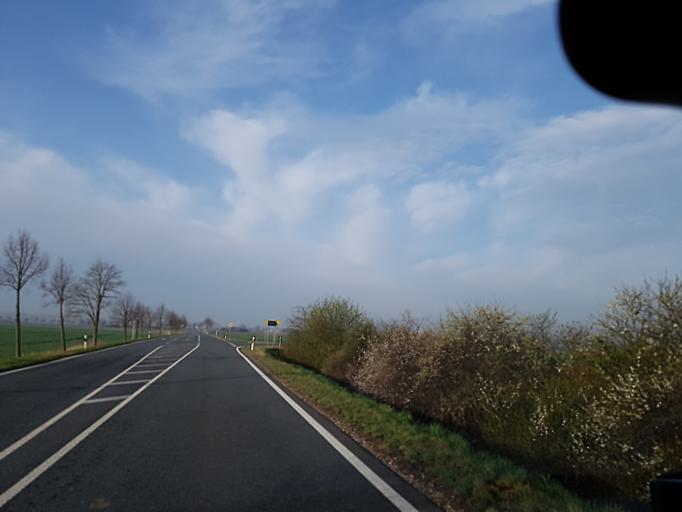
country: DE
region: Saxony
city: Strehla
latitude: 51.3644
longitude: 13.2652
